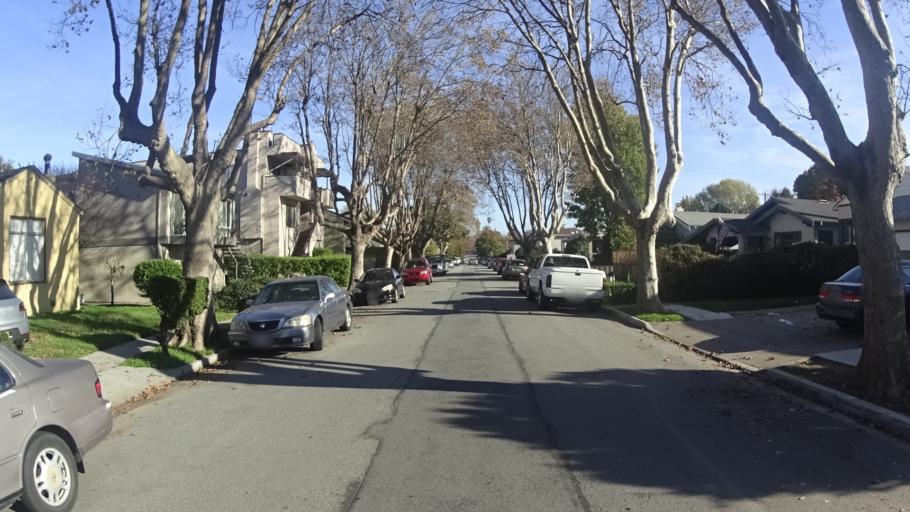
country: US
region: California
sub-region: San Mateo County
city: Burlingame
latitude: 37.5858
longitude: -122.3616
